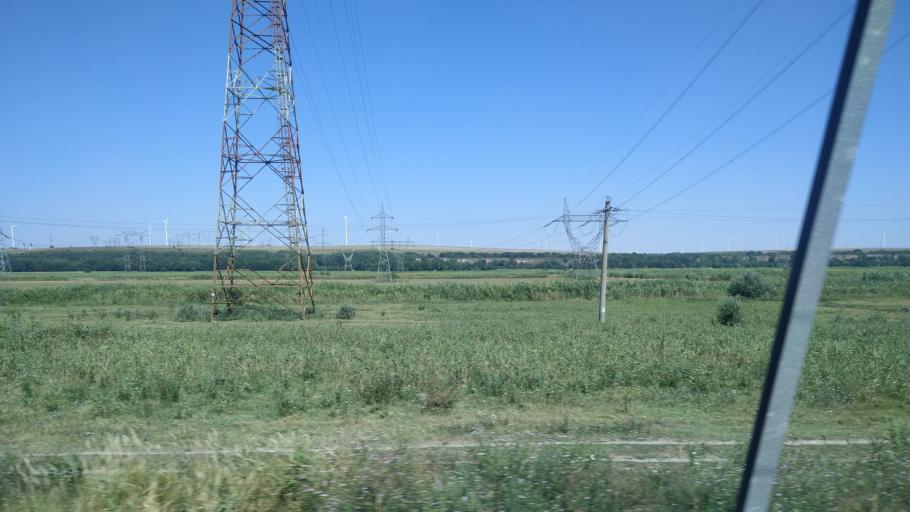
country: RO
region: Constanta
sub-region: Comuna Saligny
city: Faclia
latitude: 44.2690
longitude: 28.1263
